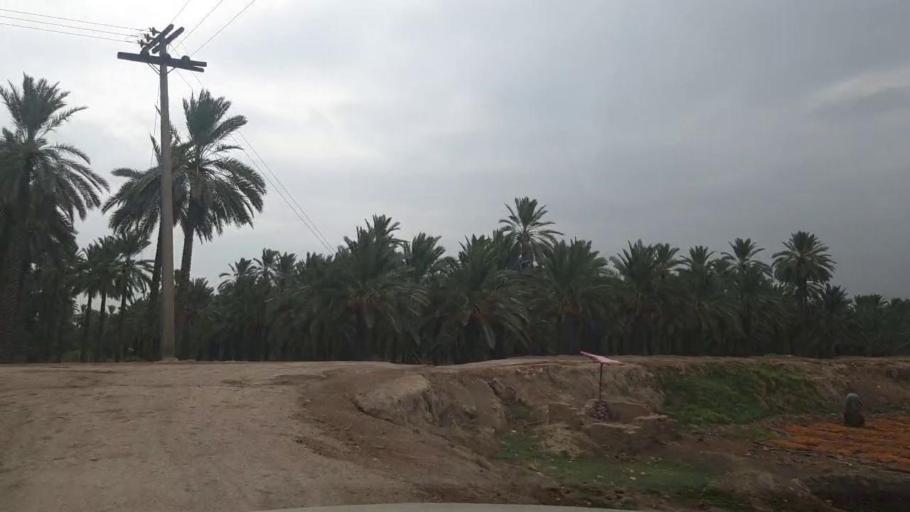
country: PK
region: Sindh
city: Khairpur
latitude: 27.6040
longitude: 68.8158
